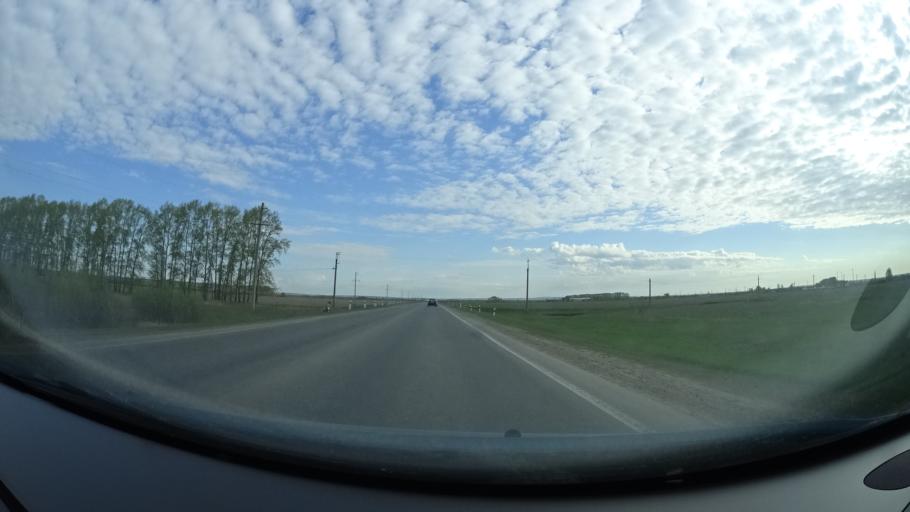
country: RU
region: Bashkortostan
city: Mikhaylovka
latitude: 54.9582
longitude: 55.7578
